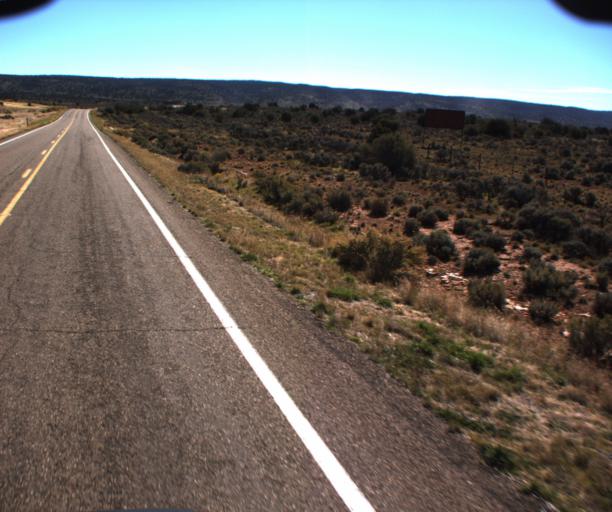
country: US
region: Arizona
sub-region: Coconino County
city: Fredonia
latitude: 36.8528
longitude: -112.2936
